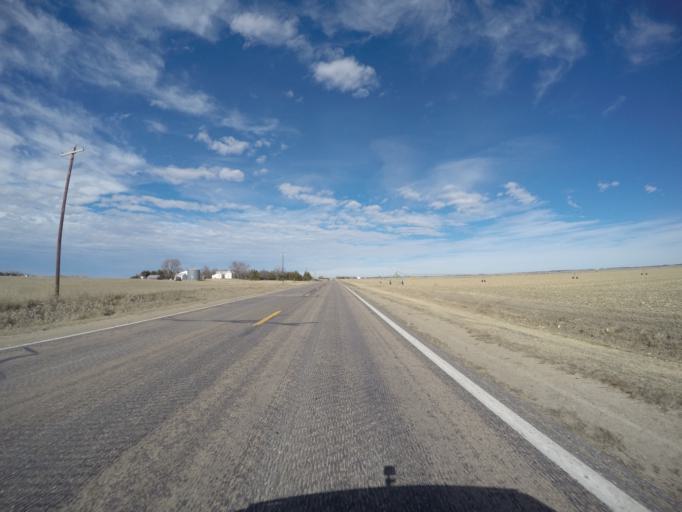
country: US
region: Nebraska
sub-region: Franklin County
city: Franklin
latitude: 40.2732
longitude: -98.9524
